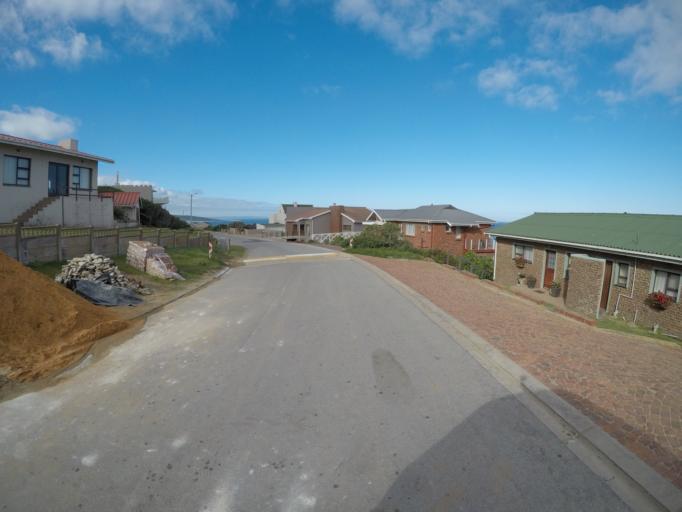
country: ZA
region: Western Cape
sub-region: Eden District Municipality
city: Riversdale
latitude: -34.4322
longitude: 21.3326
